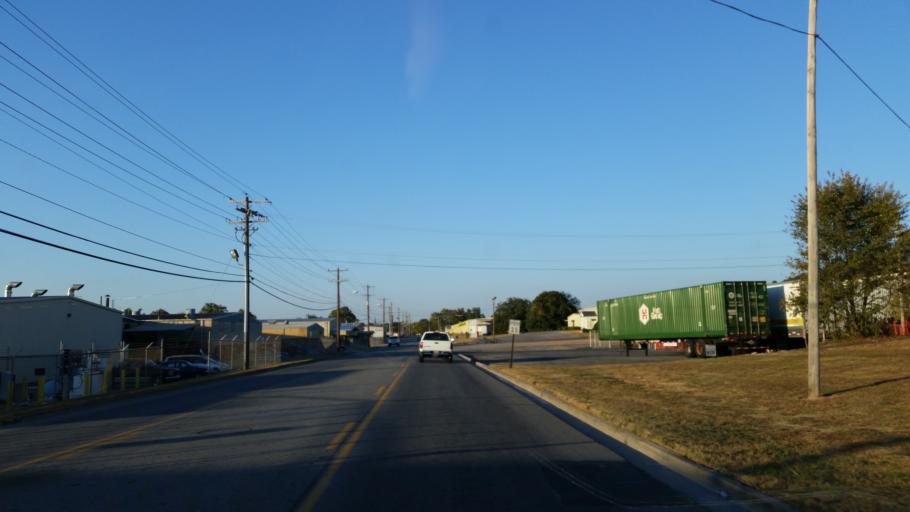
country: US
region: Georgia
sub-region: Gordon County
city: Calhoun
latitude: 34.4931
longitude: -84.9557
